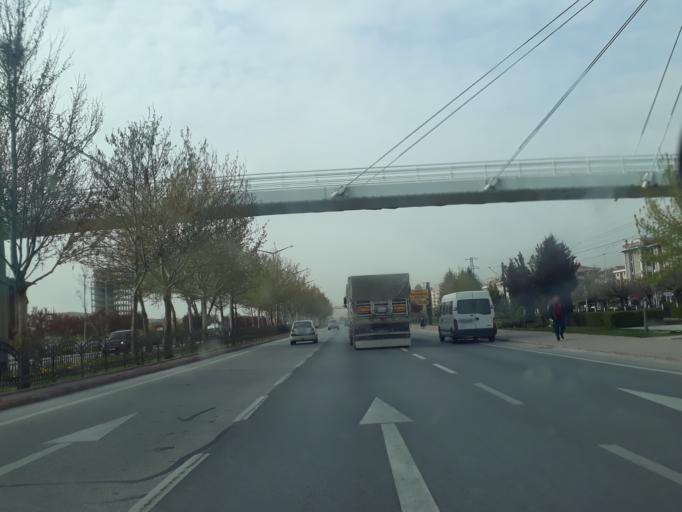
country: TR
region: Konya
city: Selcuklu
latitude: 37.9654
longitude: 32.5149
